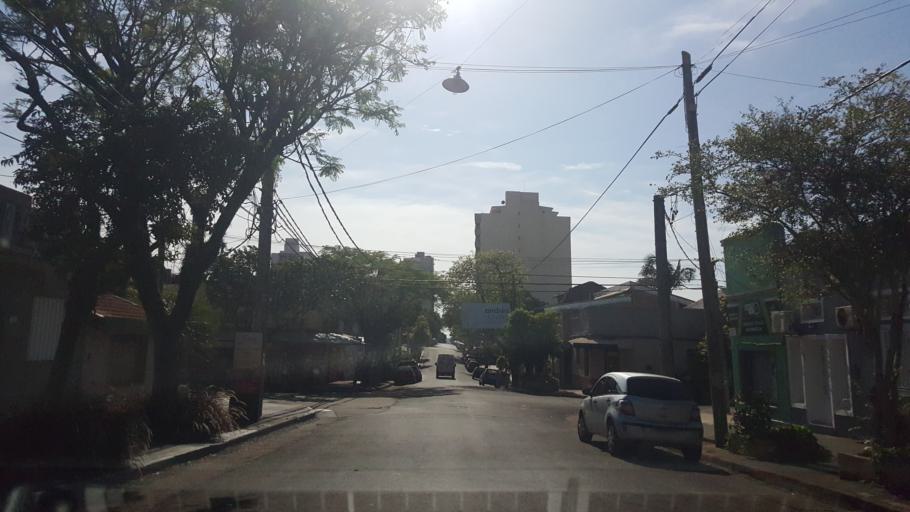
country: AR
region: Misiones
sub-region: Departamento de Capital
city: Posadas
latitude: -27.3739
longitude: -55.8918
